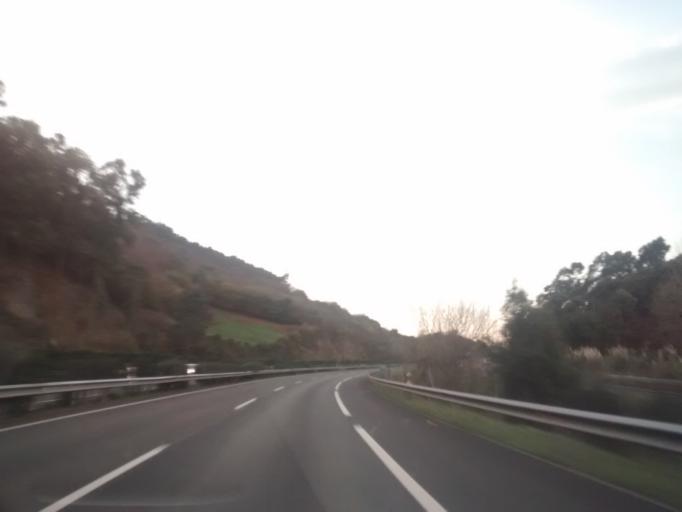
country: ES
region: Cantabria
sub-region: Provincia de Cantabria
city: Castro-Urdiales
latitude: 43.3981
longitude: -3.2761
